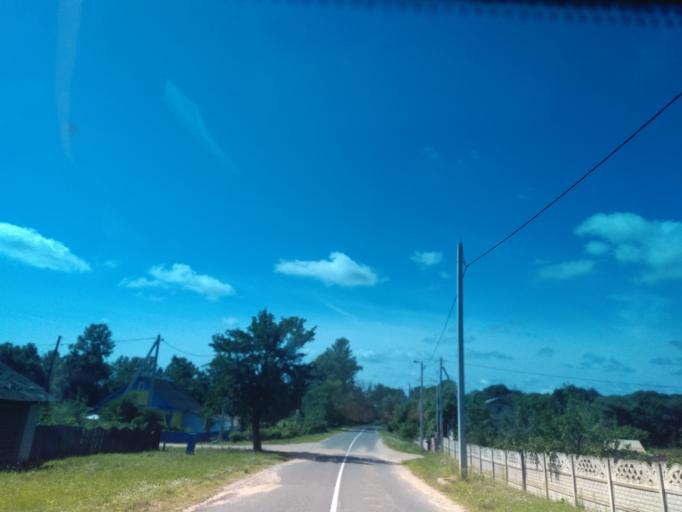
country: BY
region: Minsk
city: Uzda
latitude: 53.2881
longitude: 27.2387
